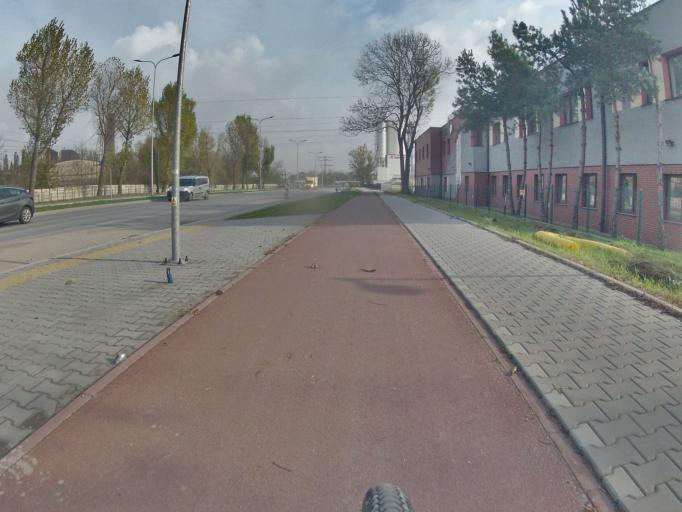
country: PL
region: Lesser Poland Voivodeship
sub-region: Powiat wielicki
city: Wegrzce Wielkie
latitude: 50.0696
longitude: 20.0958
